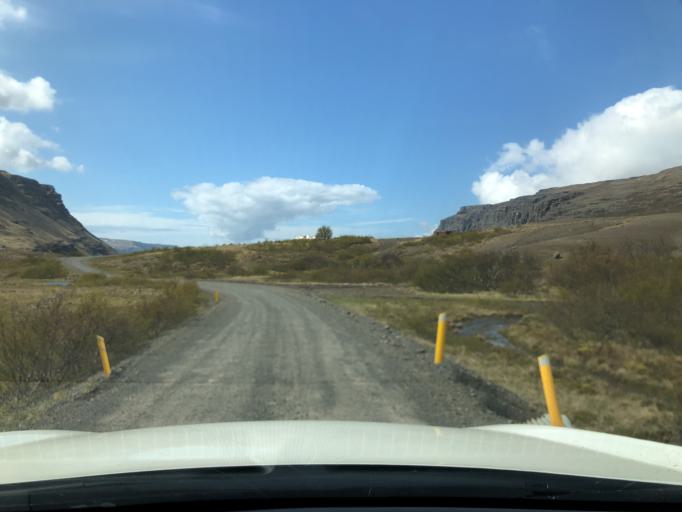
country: IS
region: South
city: Hveragerdi
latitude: 64.3855
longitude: -21.3372
